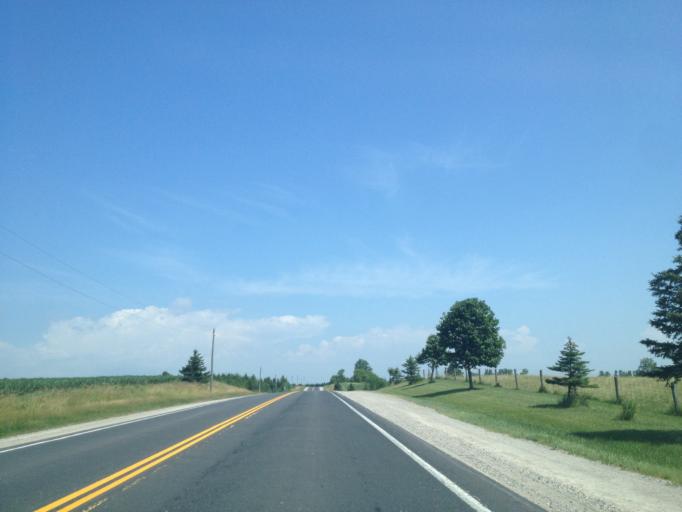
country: CA
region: Ontario
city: Huron East
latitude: 43.3934
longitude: -81.2226
